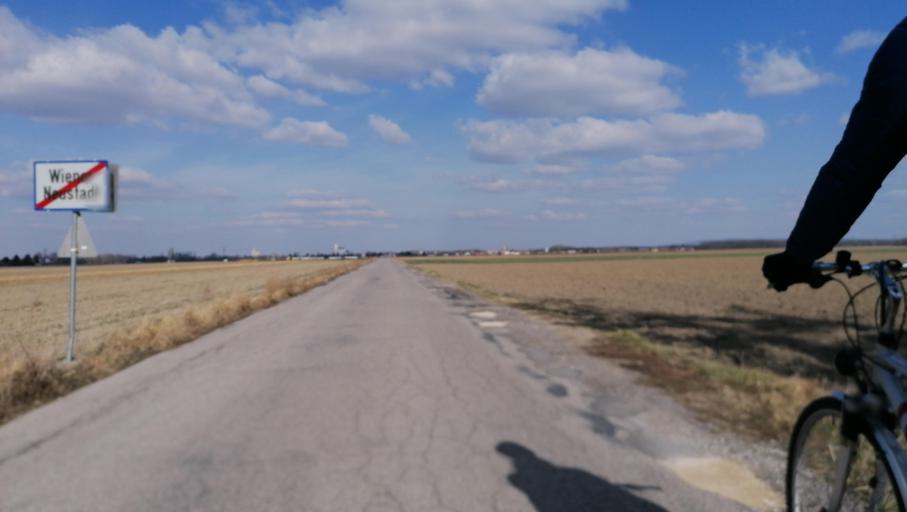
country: AT
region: Lower Austria
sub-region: Politischer Bezirk Wiener Neustadt
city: Lichtenworth
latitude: 47.8182
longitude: 16.2705
